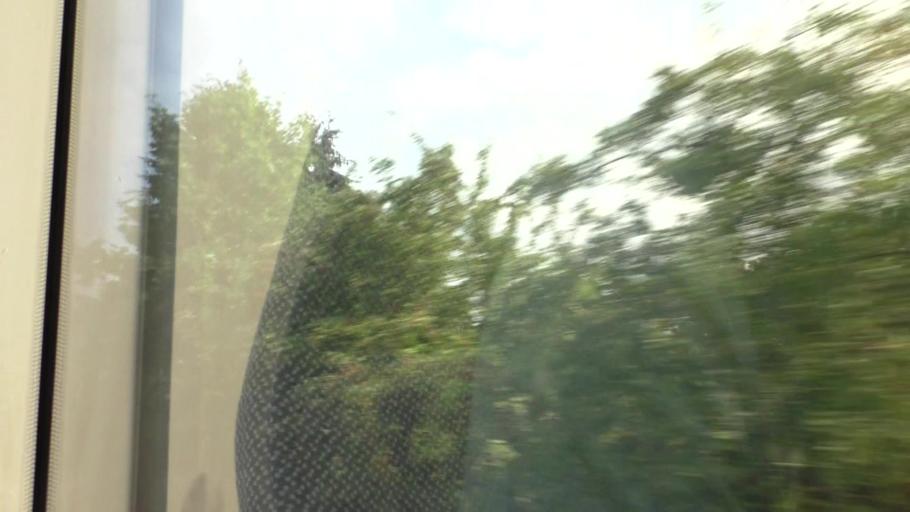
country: DE
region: Brandenburg
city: Bestensee
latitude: 52.3003
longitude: 13.7194
